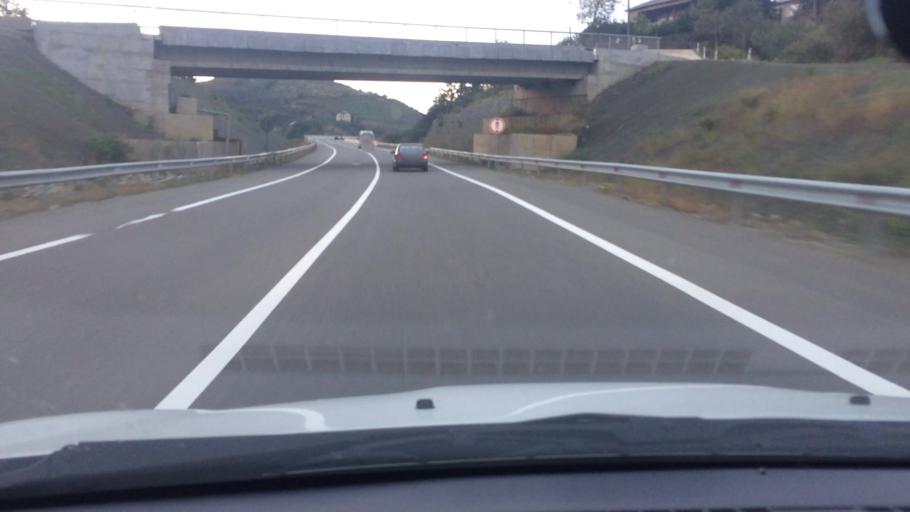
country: GE
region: Ajaria
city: Makhinjauri
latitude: 41.7181
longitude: 41.7515
